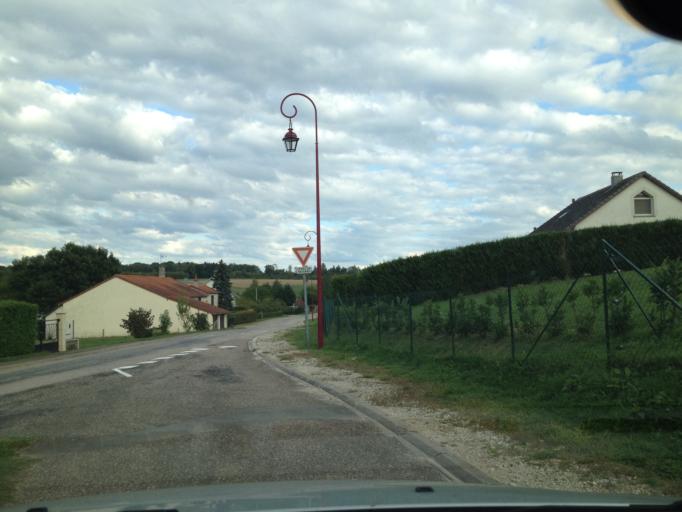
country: FR
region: Lorraine
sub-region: Departement des Vosges
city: Darney
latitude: 47.9462
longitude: 6.0985
